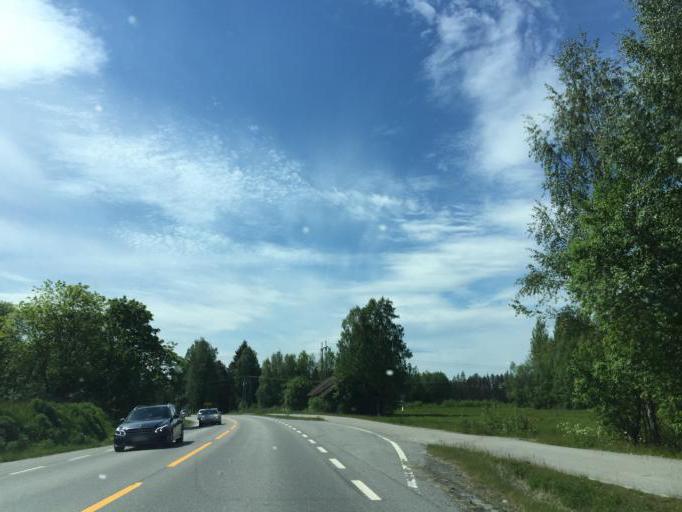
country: NO
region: Hedmark
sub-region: Sor-Odal
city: Skarnes
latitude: 60.2467
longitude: 11.6685
